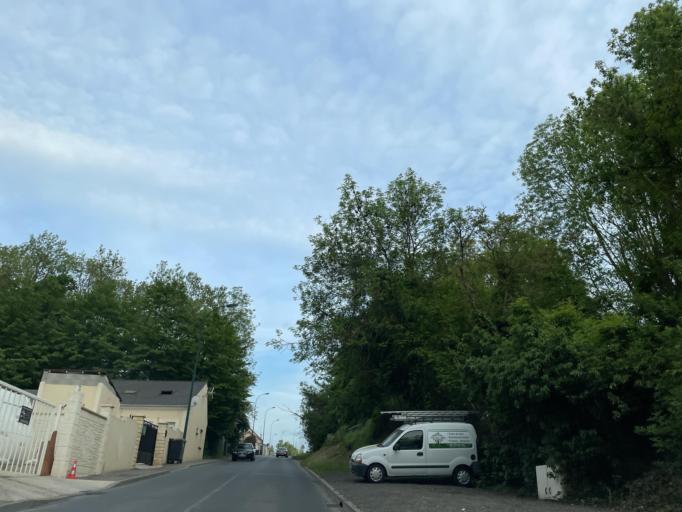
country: FR
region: Ile-de-France
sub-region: Departement de Seine-et-Marne
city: Nanteuil-les-Meaux
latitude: 48.9305
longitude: 2.8817
